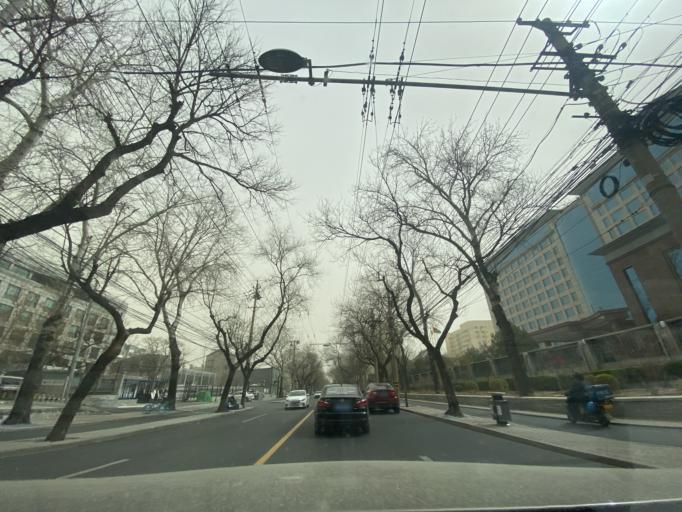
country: CN
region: Beijing
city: Jinrongjie
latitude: 39.9391
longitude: 116.3542
